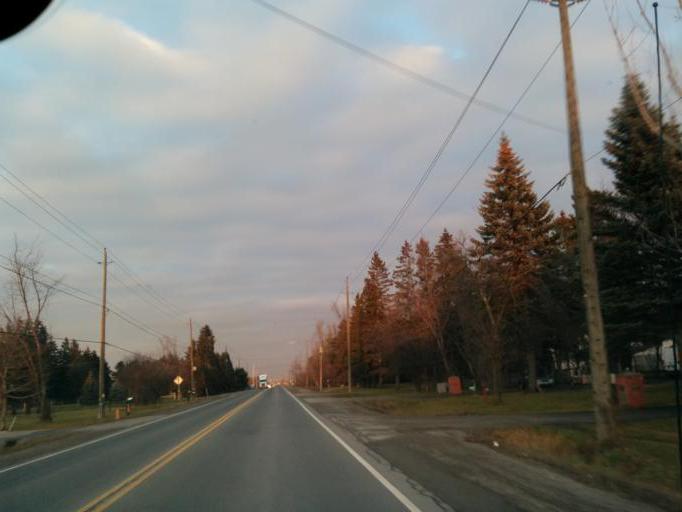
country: CA
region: Ontario
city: Brampton
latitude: 43.8234
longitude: -79.7231
